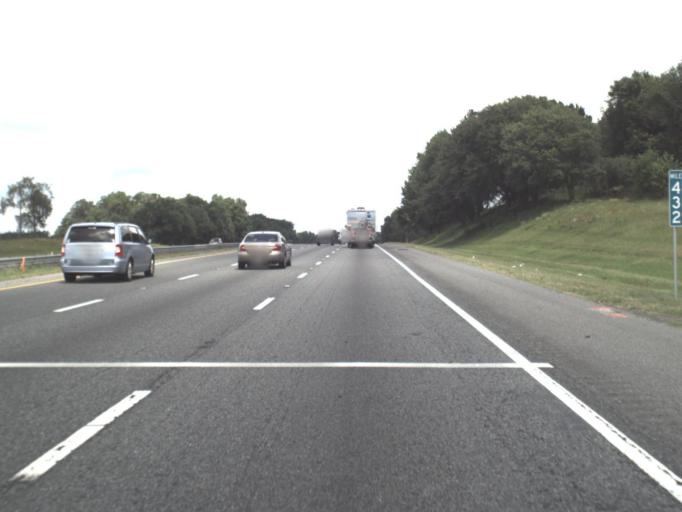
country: US
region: Florida
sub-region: Suwannee County
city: Wellborn
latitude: 30.2334
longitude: -82.7297
